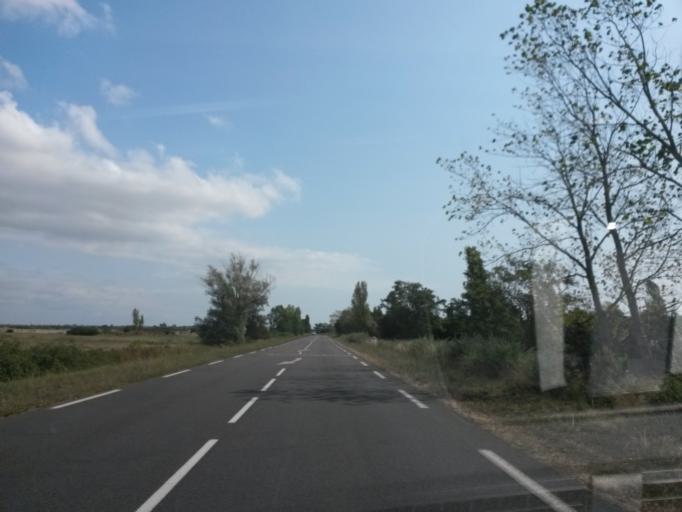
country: FR
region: Pays de la Loire
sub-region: Departement de la Vendee
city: La Tranche-sur-Mer
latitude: 46.3597
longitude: -1.4477
